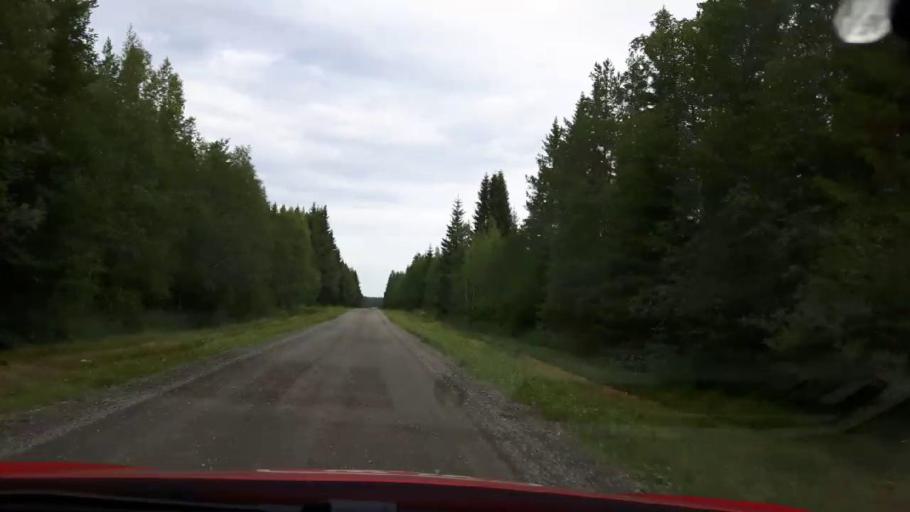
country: SE
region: Jaemtland
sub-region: Stroemsunds Kommun
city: Stroemsund
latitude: 63.7274
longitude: 15.5453
